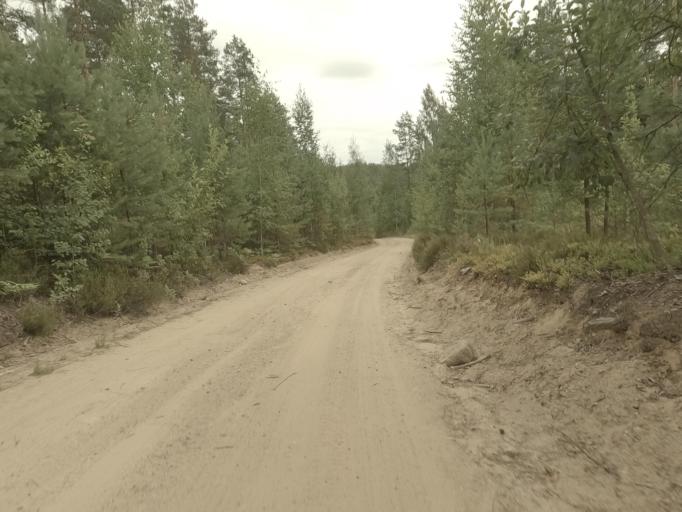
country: RU
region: Leningrad
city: Kamennogorsk
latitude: 61.0005
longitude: 29.1807
